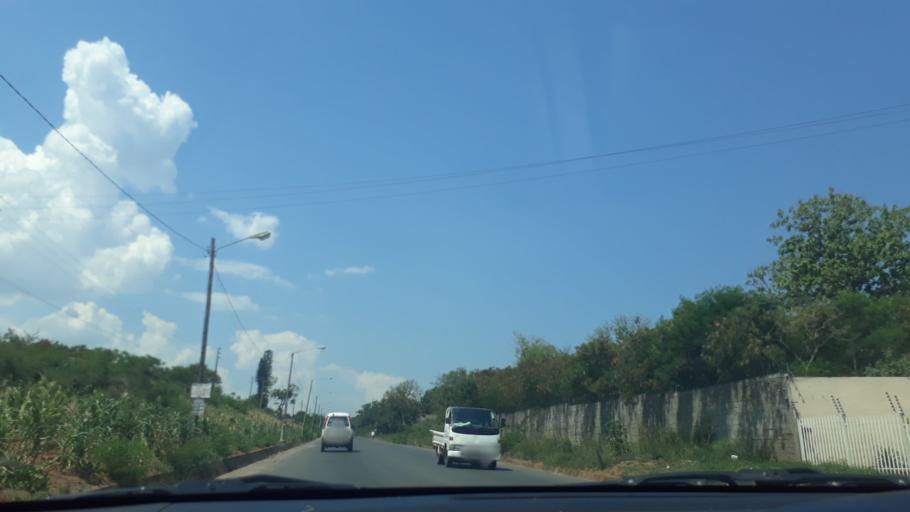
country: MZ
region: Maputo
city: Matola
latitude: -25.9644
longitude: 32.4464
